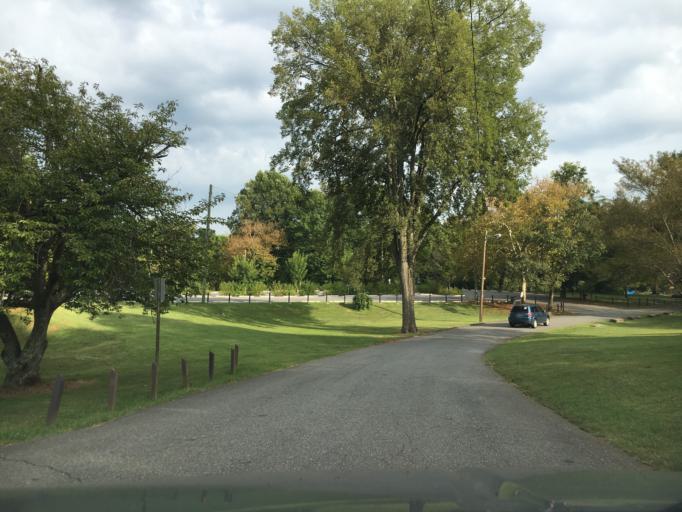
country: US
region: Virginia
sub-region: City of Lynchburg
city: Lynchburg
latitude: 37.4381
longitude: -79.1636
